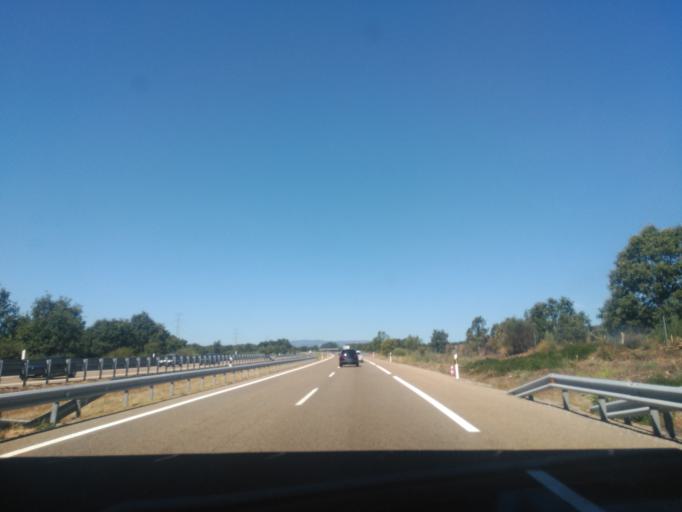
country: ES
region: Castille and Leon
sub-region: Provincia de Zamora
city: Cernadilla
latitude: 42.0382
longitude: -6.4453
